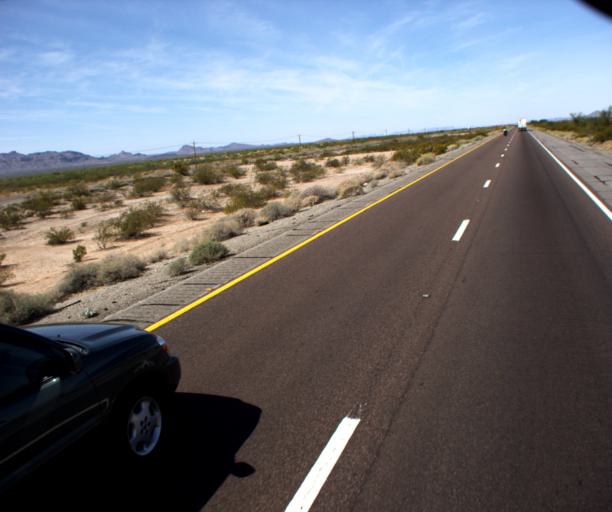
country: US
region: Arizona
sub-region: La Paz County
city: Salome
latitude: 33.5631
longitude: -113.3122
